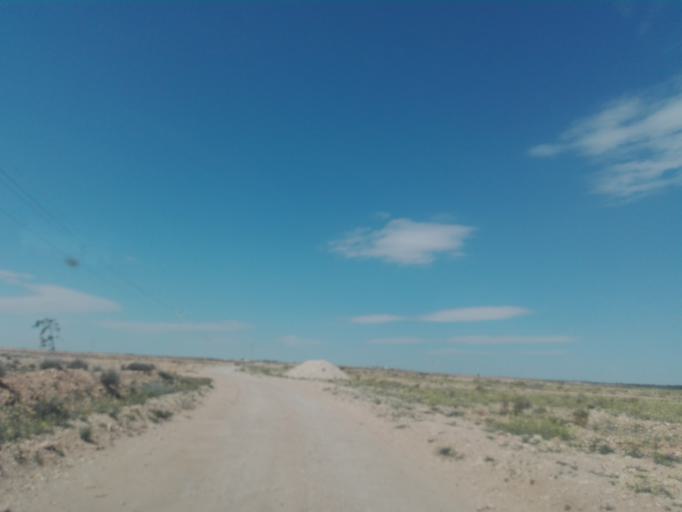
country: TN
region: Safaqis
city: Sfax
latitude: 34.6872
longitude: 10.5472
